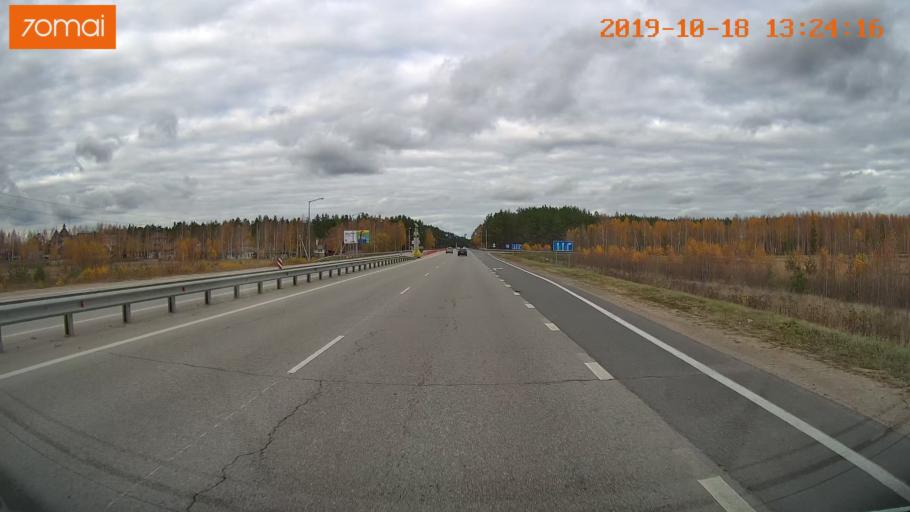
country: RU
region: Rjazan
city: Polyany
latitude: 54.7284
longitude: 39.8449
